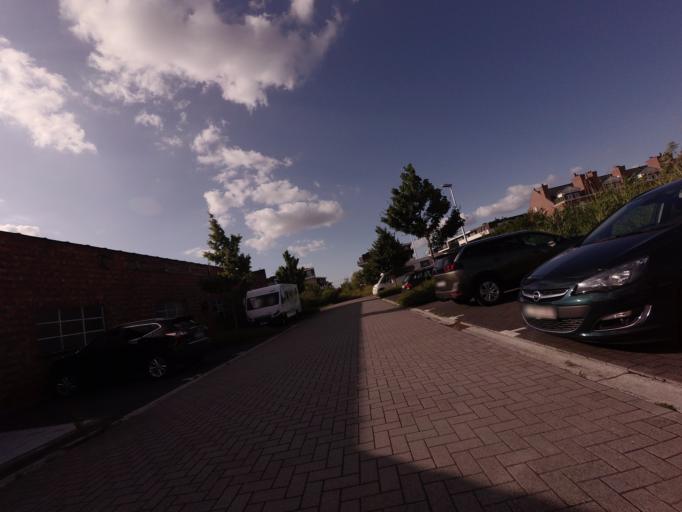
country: BE
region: Flanders
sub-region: Provincie Antwerpen
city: Edegem
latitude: 51.1553
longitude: 4.4247
